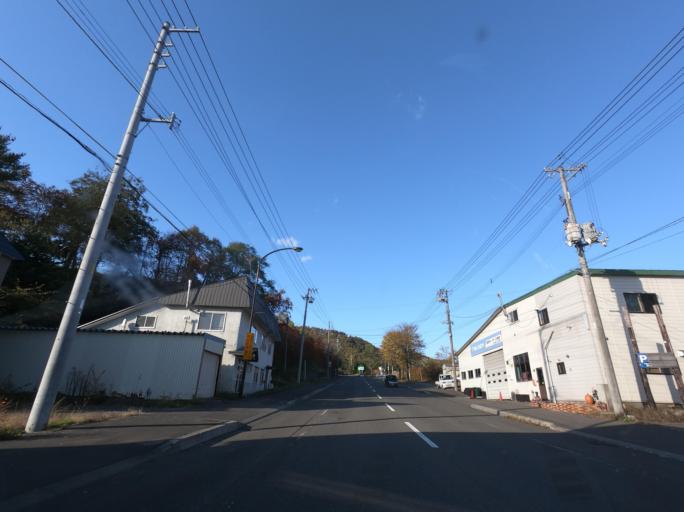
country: JP
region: Hokkaido
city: Iwamizawa
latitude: 43.0431
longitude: 141.9628
